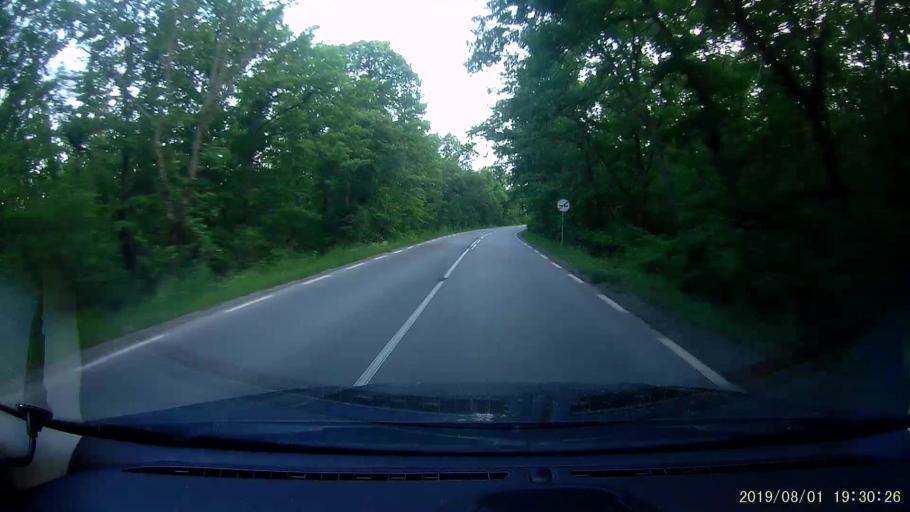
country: BG
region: Burgas
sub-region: Obshtina Sungurlare
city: Sungurlare
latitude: 42.8138
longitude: 26.8930
